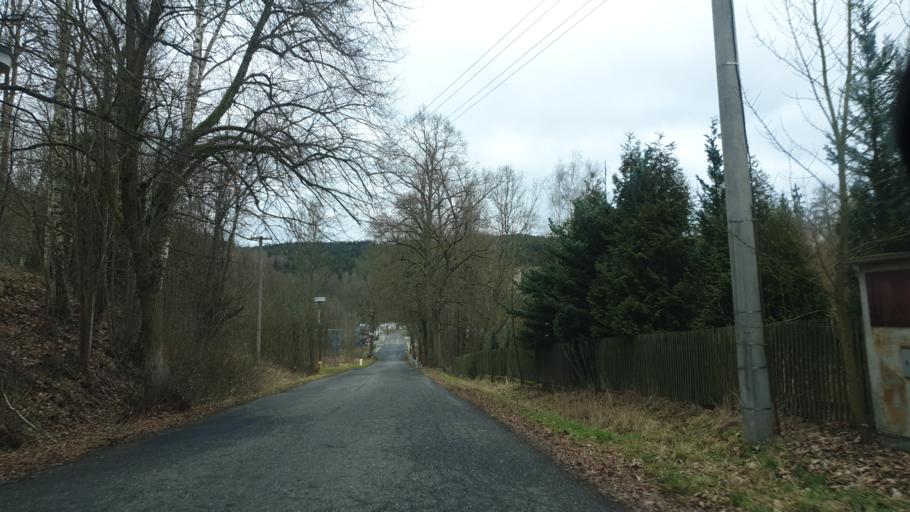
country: DE
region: Saxony
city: Bad Elster
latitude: 50.2638
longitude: 12.2441
